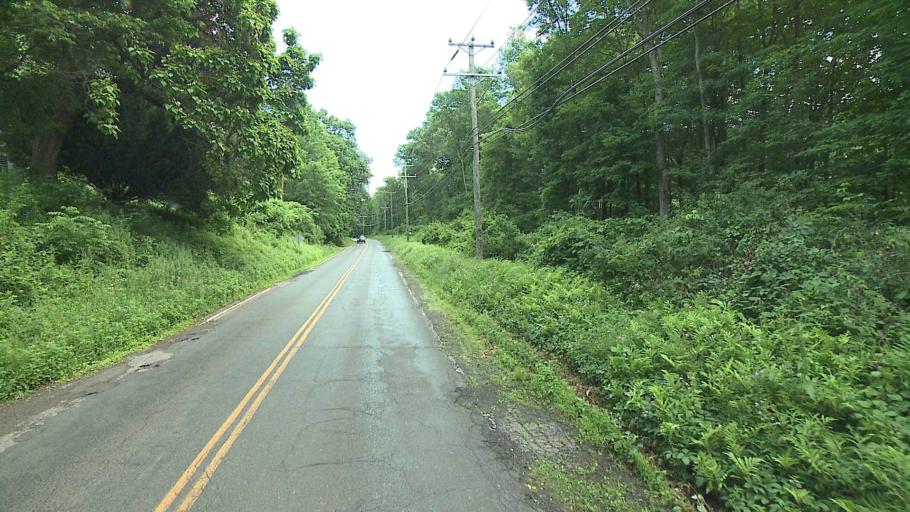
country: US
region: Connecticut
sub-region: Litchfield County
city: Kent
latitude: 41.7012
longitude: -73.4804
